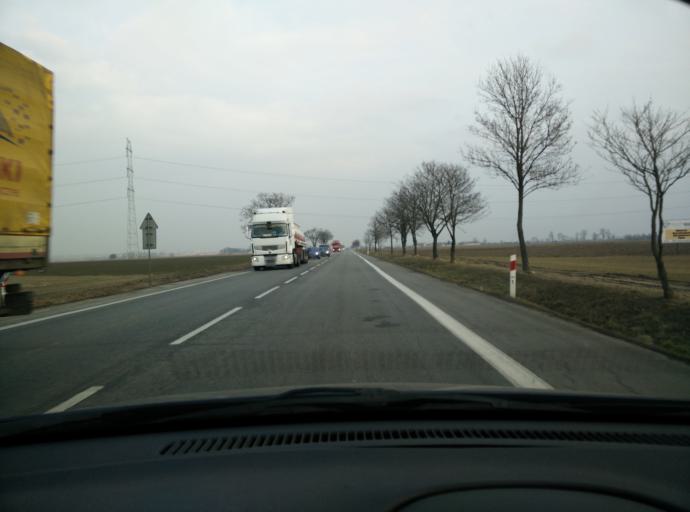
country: PL
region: Greater Poland Voivodeship
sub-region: Powiat sredzki
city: Sroda Wielkopolska
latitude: 52.2298
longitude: 17.2050
